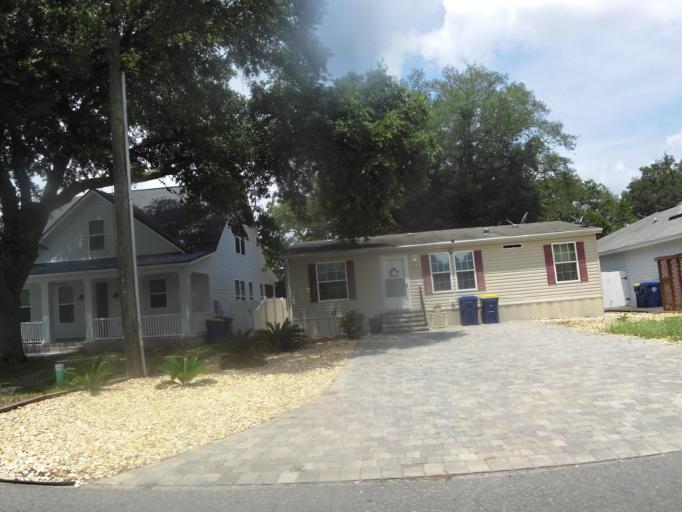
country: US
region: Florida
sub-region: Nassau County
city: Fernandina Beach
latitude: 30.6625
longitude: -81.4584
